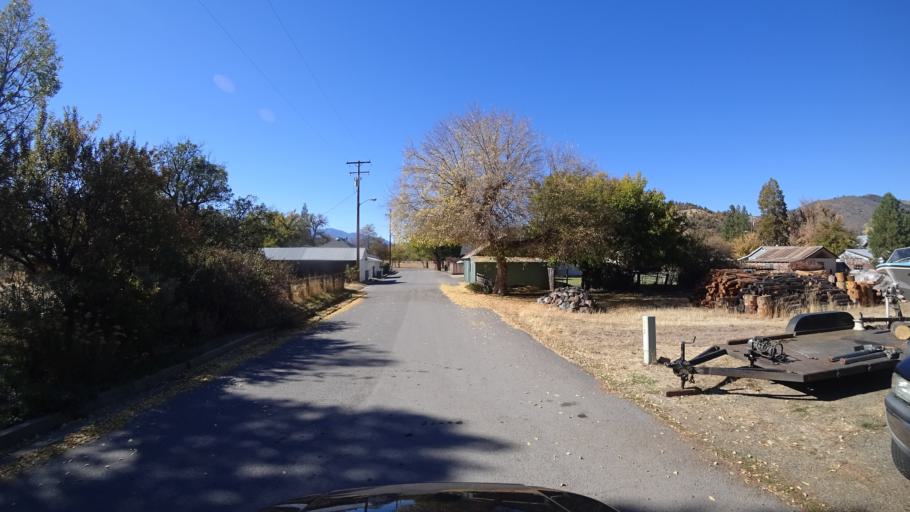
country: US
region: California
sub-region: Siskiyou County
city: Yreka
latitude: 41.6114
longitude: -122.8380
